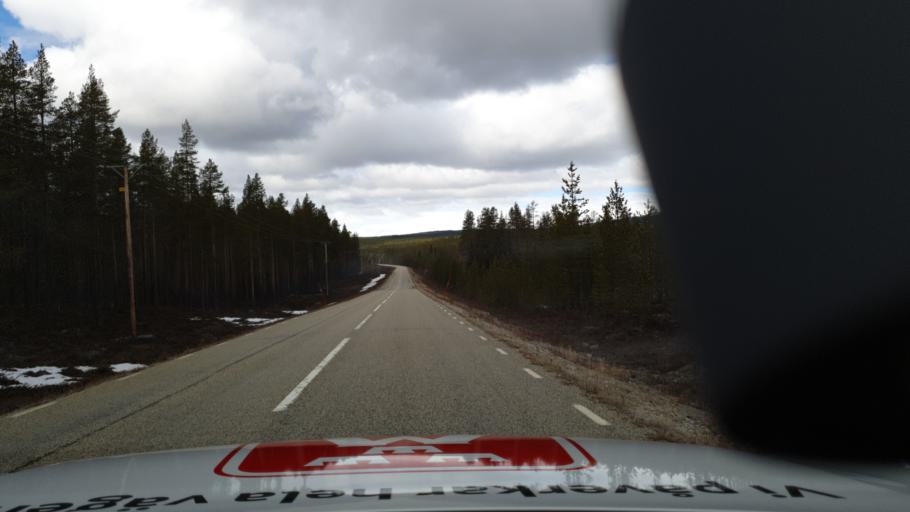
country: SE
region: Jaemtland
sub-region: Are Kommun
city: Jarpen
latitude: 62.8043
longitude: 13.6651
